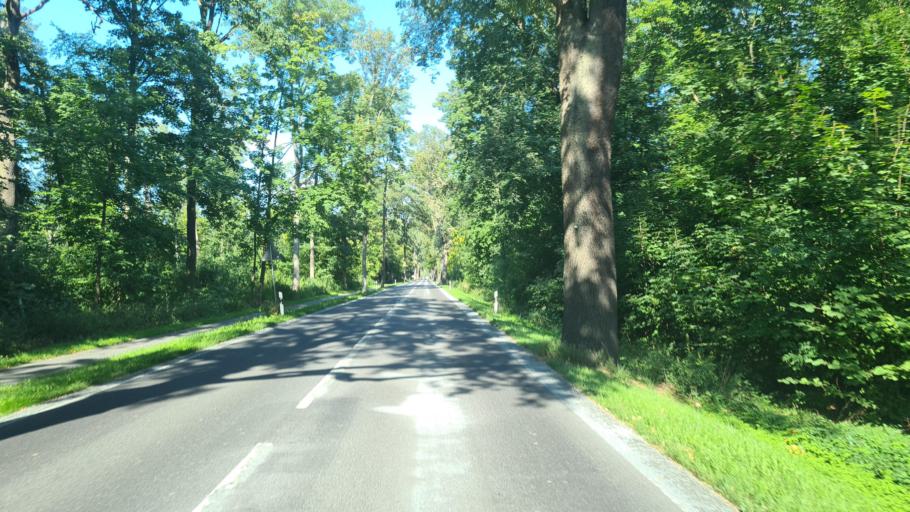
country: DE
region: Brandenburg
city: Nauen
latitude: 52.6653
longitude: 12.9267
